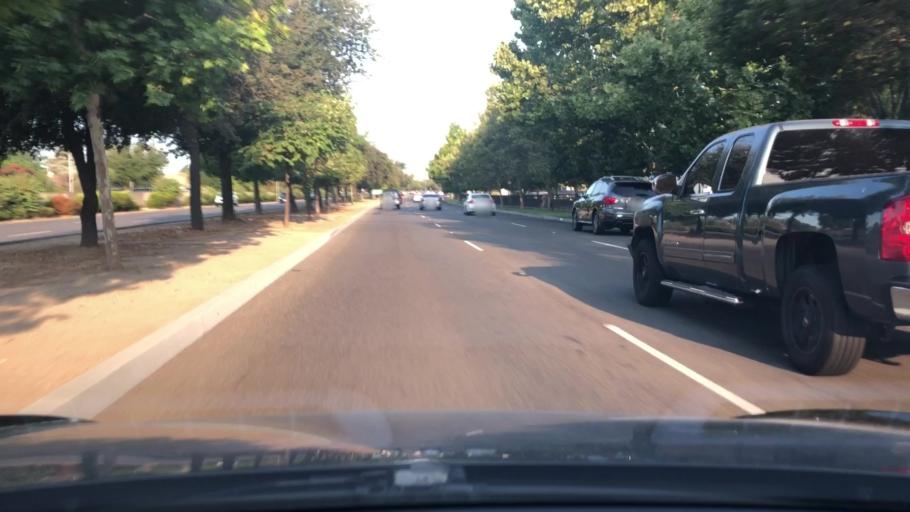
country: US
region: California
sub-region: Fresno County
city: Clovis
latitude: 36.8375
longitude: -119.7496
